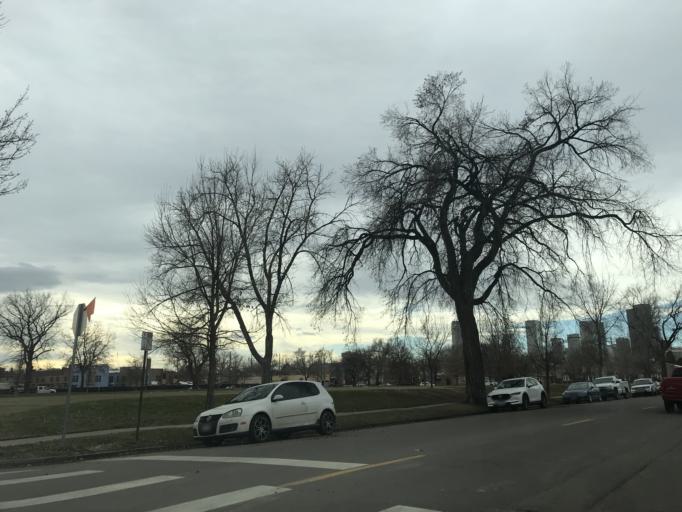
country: US
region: Colorado
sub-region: Denver County
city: Denver
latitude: 39.7613
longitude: -104.9768
